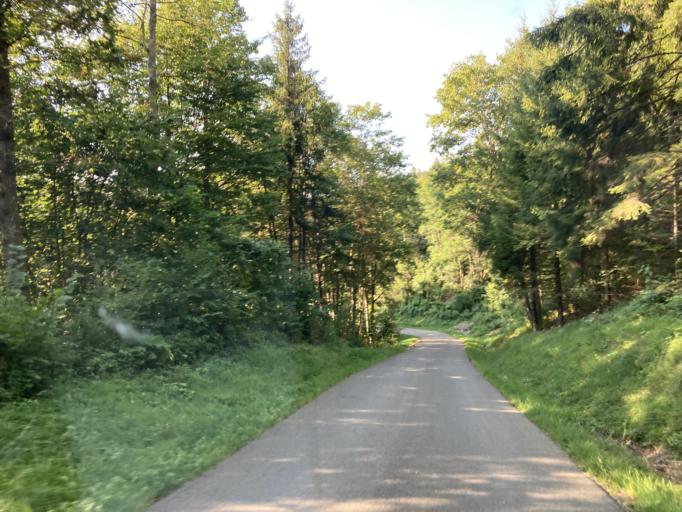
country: DE
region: Baden-Wuerttemberg
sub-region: Freiburg Region
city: Blumberg
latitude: 47.8175
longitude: 8.5134
